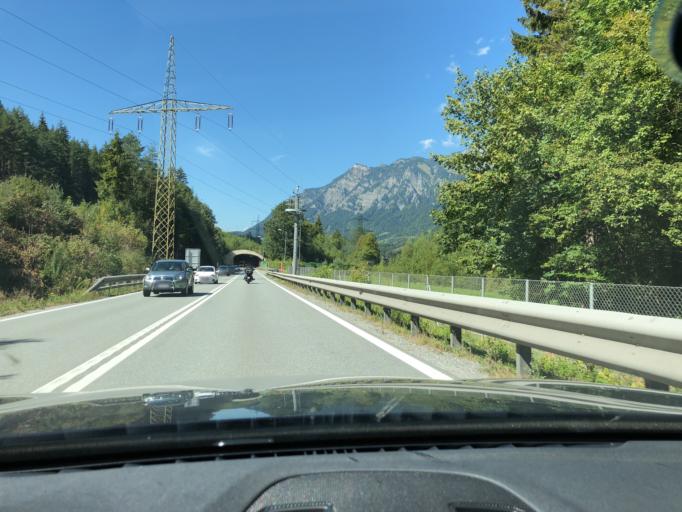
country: AT
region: Vorarlberg
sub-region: Politischer Bezirk Bludenz
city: Innerbraz
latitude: 47.1349
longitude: 9.9435
